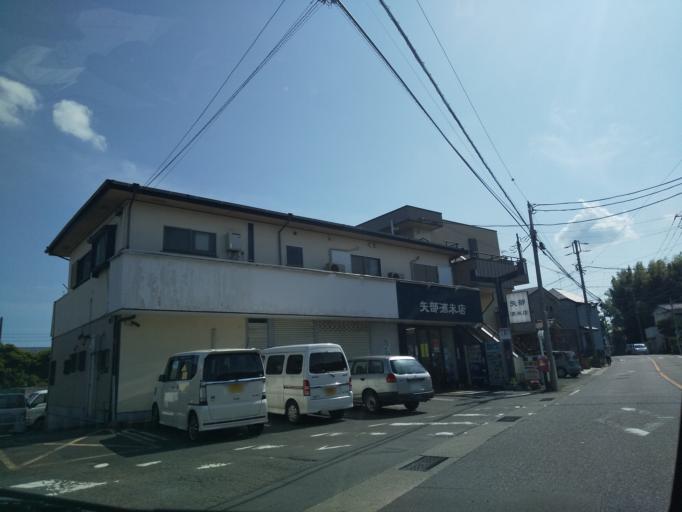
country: JP
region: Kanagawa
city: Zama
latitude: 35.4577
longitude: 139.4110
